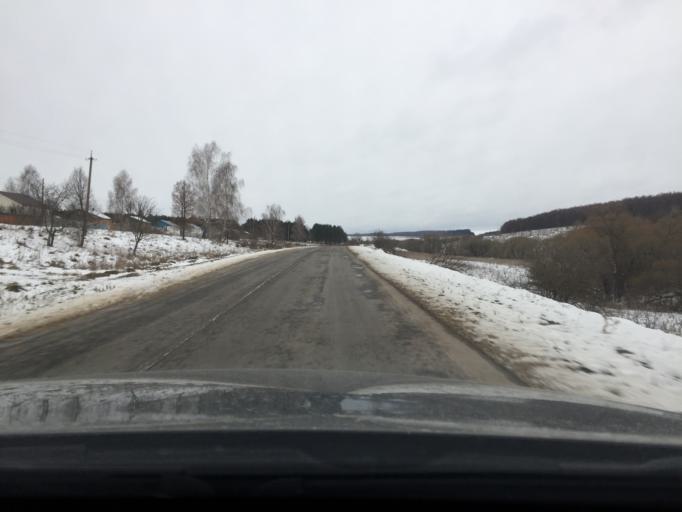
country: RU
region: Tula
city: Shchekino
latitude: 53.8252
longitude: 37.5586
